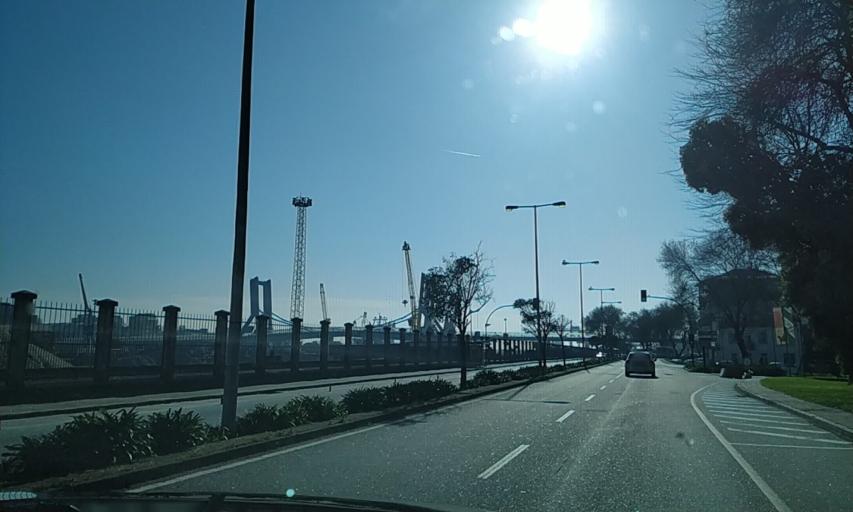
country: PT
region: Porto
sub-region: Matosinhos
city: Leca da Palmeira
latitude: 41.1917
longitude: -8.6922
